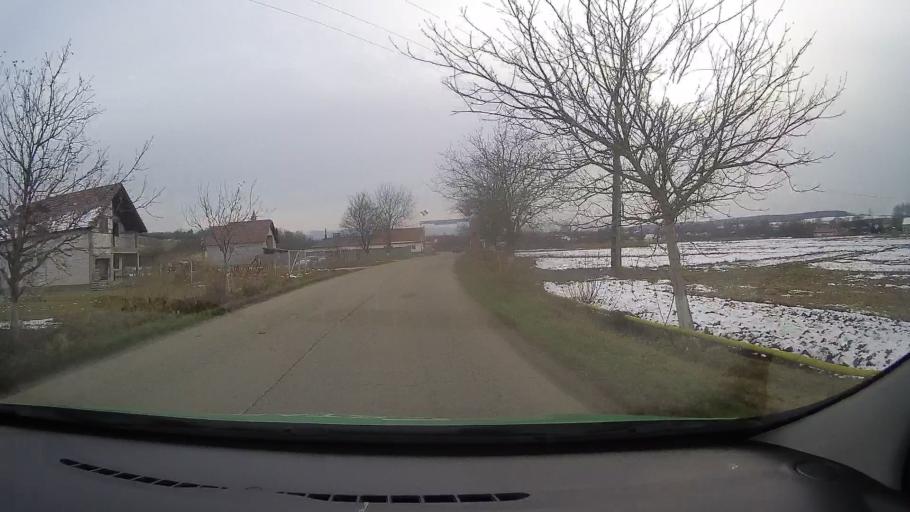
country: RO
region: Hunedoara
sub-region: Comuna Romos
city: Romos
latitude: 45.8532
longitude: 23.2738
